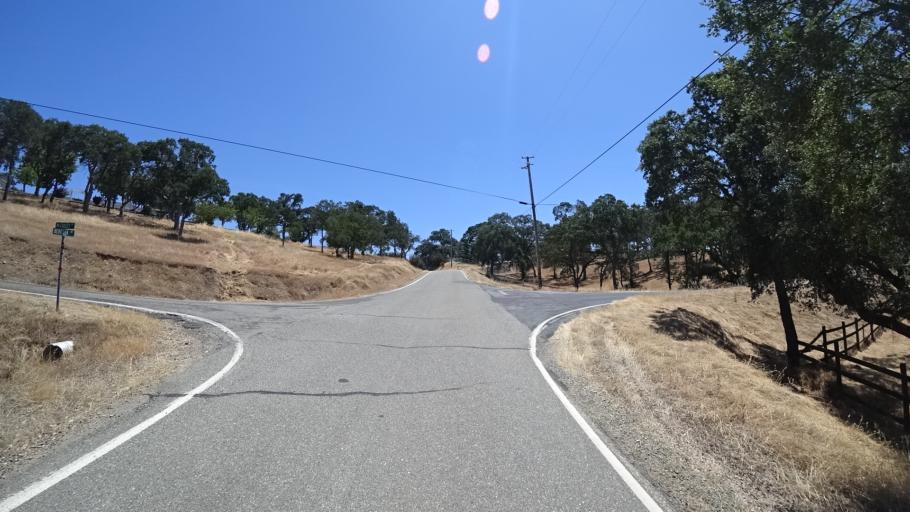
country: US
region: California
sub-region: Calaveras County
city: Rancho Calaveras
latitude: 38.1297
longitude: -120.8544
